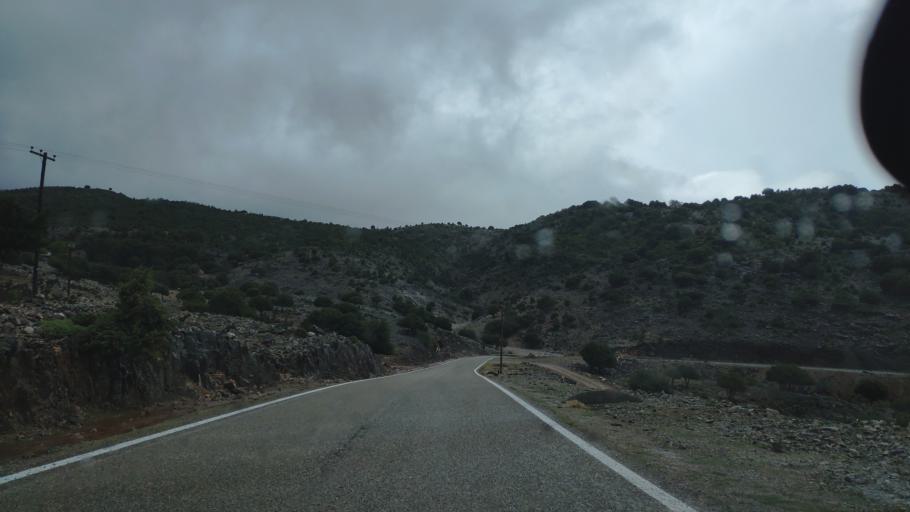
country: GR
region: West Greece
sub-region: Nomos Aitolias kai Akarnanias
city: Krikellos
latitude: 39.0781
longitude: 21.3982
